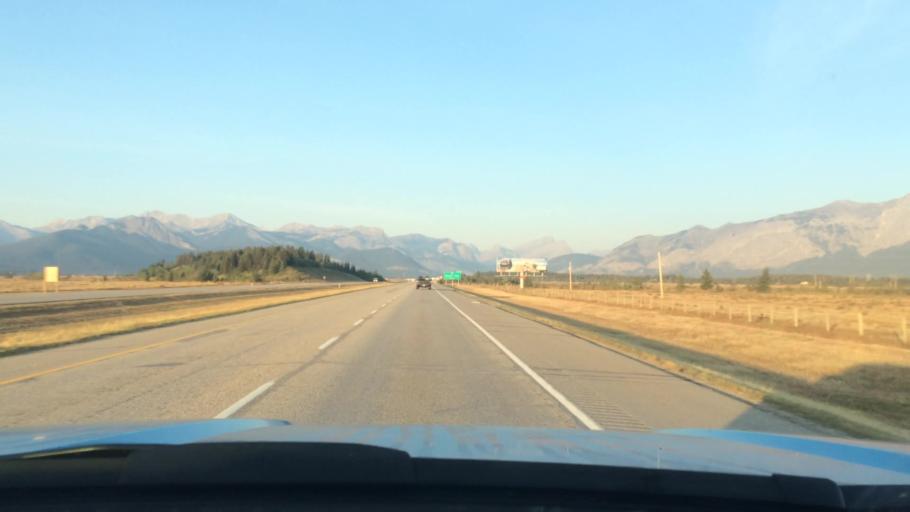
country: CA
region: Alberta
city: Canmore
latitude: 51.1175
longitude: -114.9867
